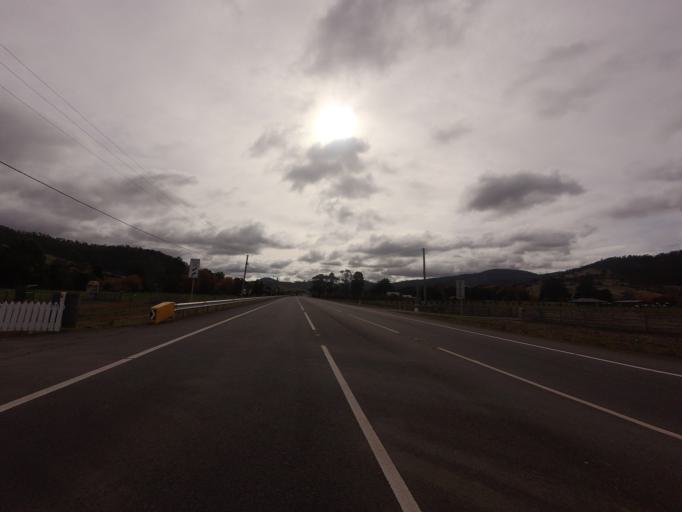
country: AU
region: Tasmania
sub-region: Brighton
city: Bridgewater
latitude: -42.6106
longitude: 147.2222
